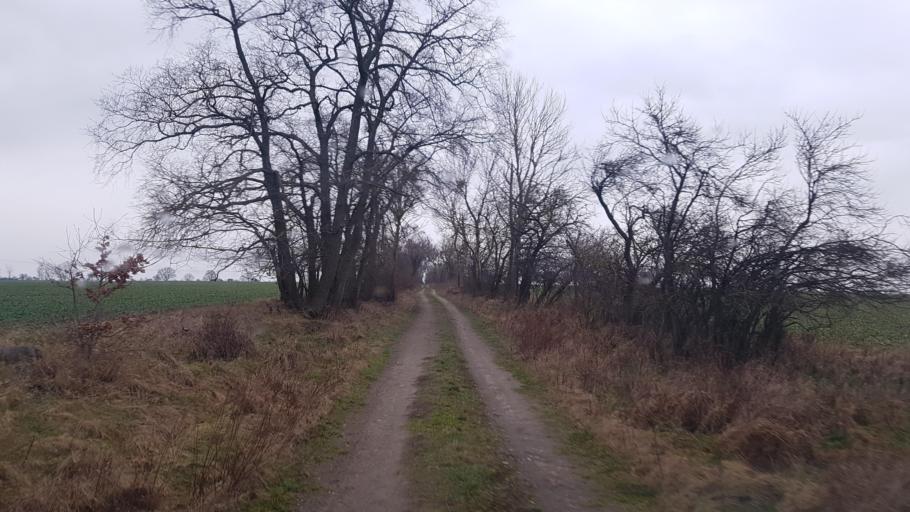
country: DE
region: Brandenburg
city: Zehdenick
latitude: 52.9489
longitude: 13.2558
